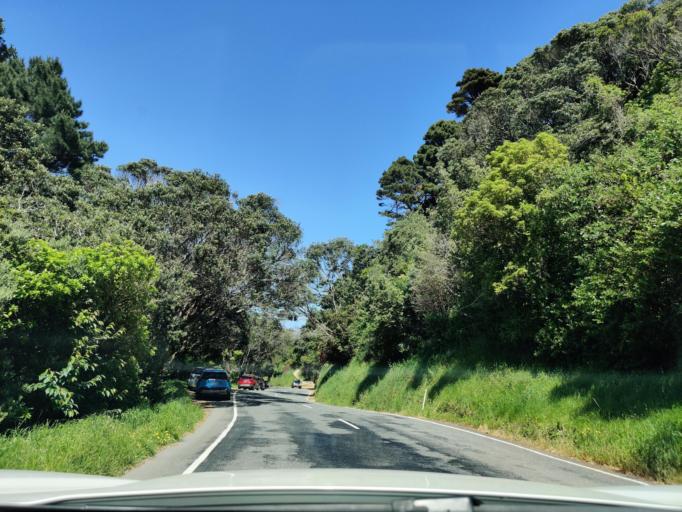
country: NZ
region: Wellington
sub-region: Wellington City
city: Wellington
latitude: -41.3037
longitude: 174.7890
